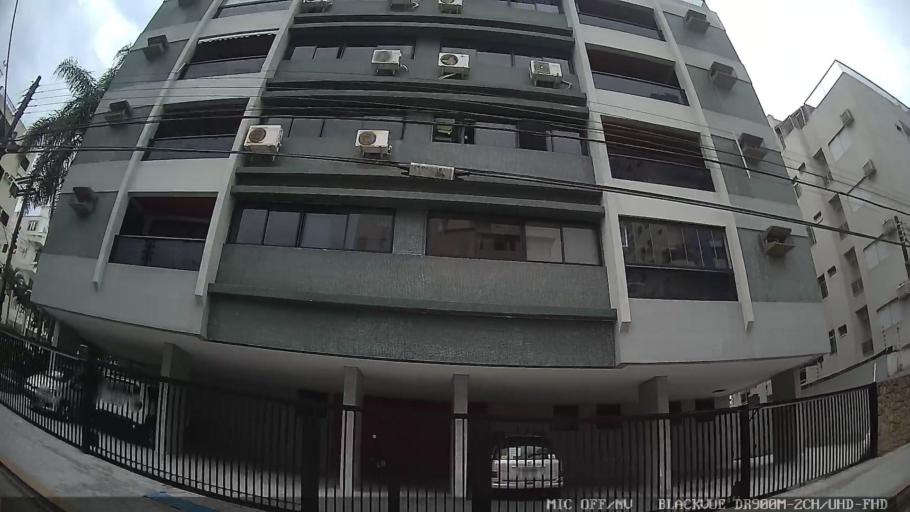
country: BR
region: Sao Paulo
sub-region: Guaruja
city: Guaruja
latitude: -23.9820
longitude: -46.2250
